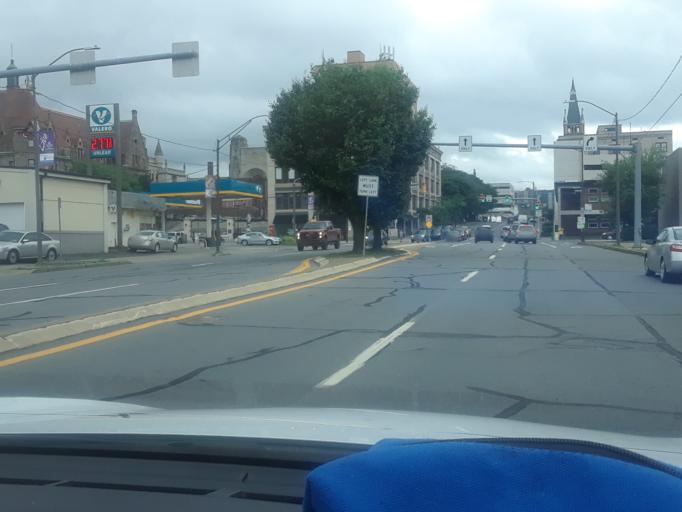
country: US
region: Pennsylvania
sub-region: Lackawanna County
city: Scranton
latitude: 41.4117
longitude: -75.6635
